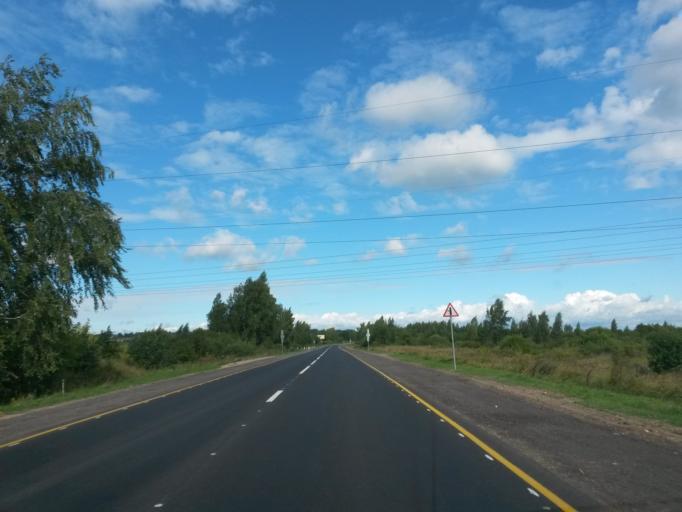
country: RU
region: Jaroslavl
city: Yaroslavl
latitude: 57.5266
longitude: 39.8793
